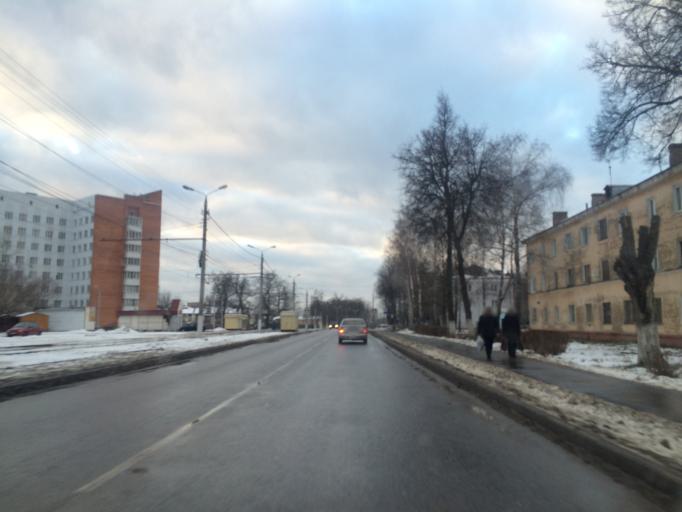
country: RU
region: Tula
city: Tula
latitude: 54.2196
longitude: 37.6990
